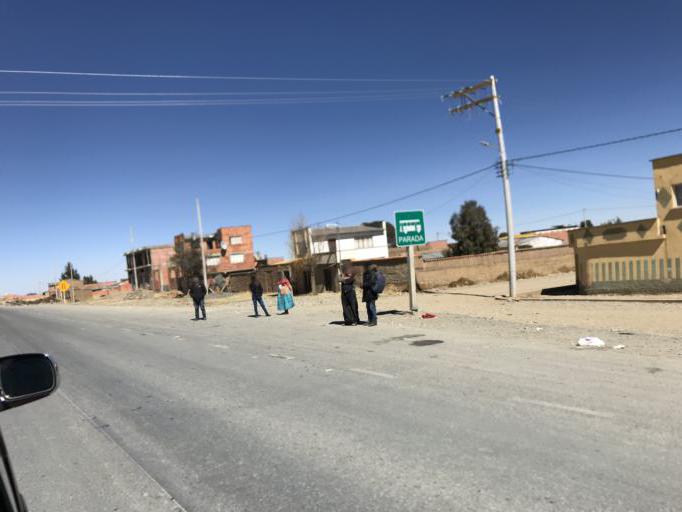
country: BO
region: La Paz
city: Batallas
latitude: -16.3362
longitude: -68.4154
